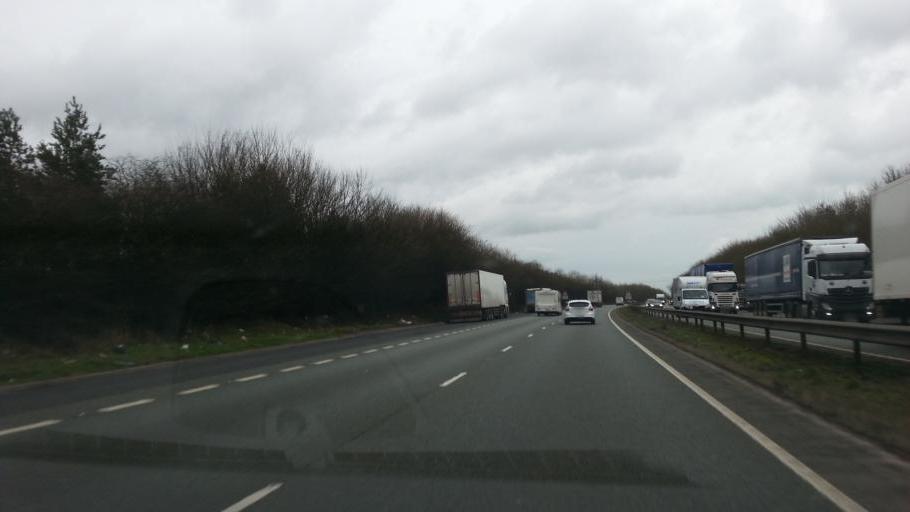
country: GB
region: England
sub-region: Leicestershire
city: Market Harborough
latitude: 52.4070
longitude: -0.9591
